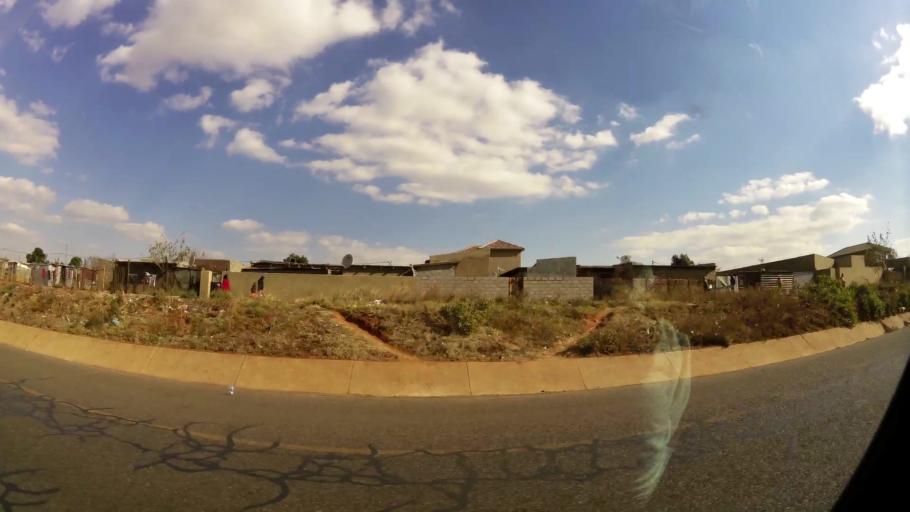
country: ZA
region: Gauteng
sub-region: Ekurhuleni Metropolitan Municipality
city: Tembisa
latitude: -25.9696
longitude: 28.2212
